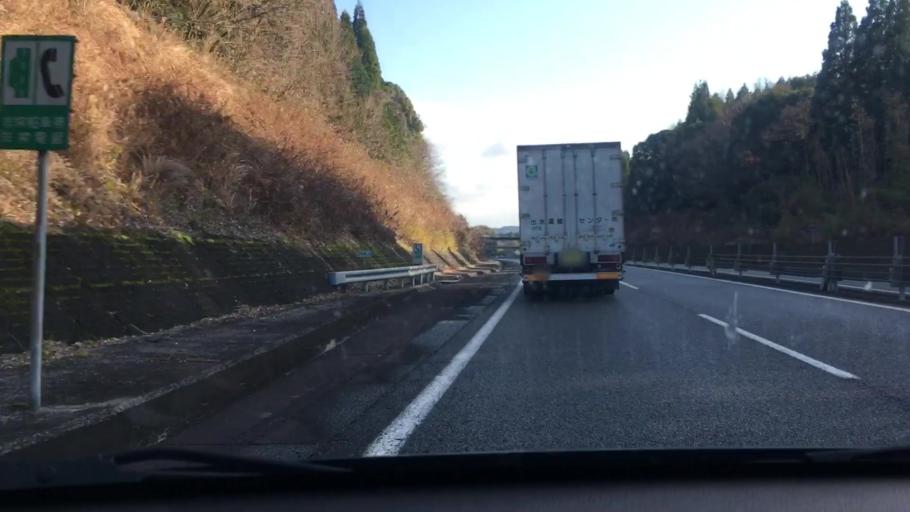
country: JP
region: Kagoshima
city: Okuchi-shinohara
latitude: 31.9128
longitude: 130.7042
